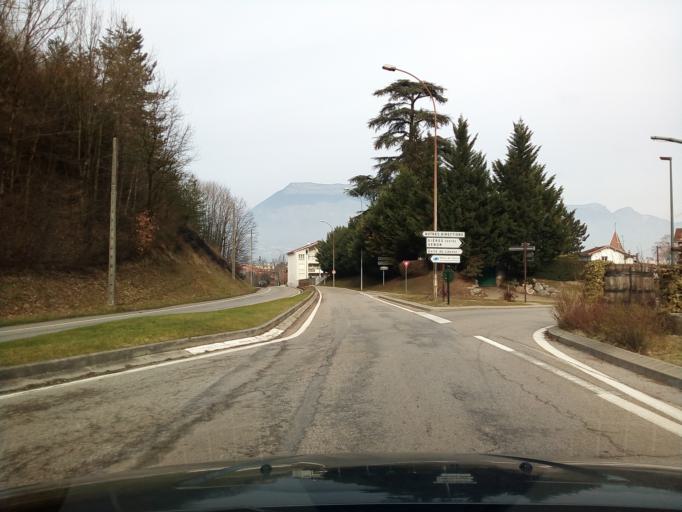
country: FR
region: Rhone-Alpes
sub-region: Departement de l'Isere
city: Gieres
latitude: 45.1780
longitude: 5.7900
